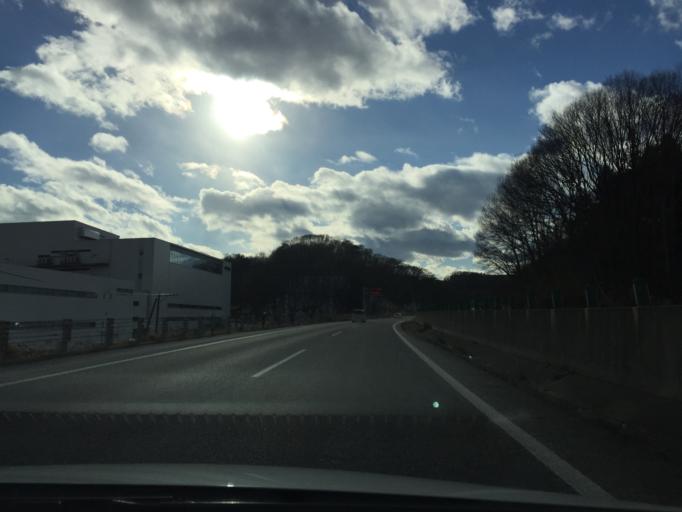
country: JP
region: Tochigi
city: Kuroiso
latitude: 37.1195
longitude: 140.1718
